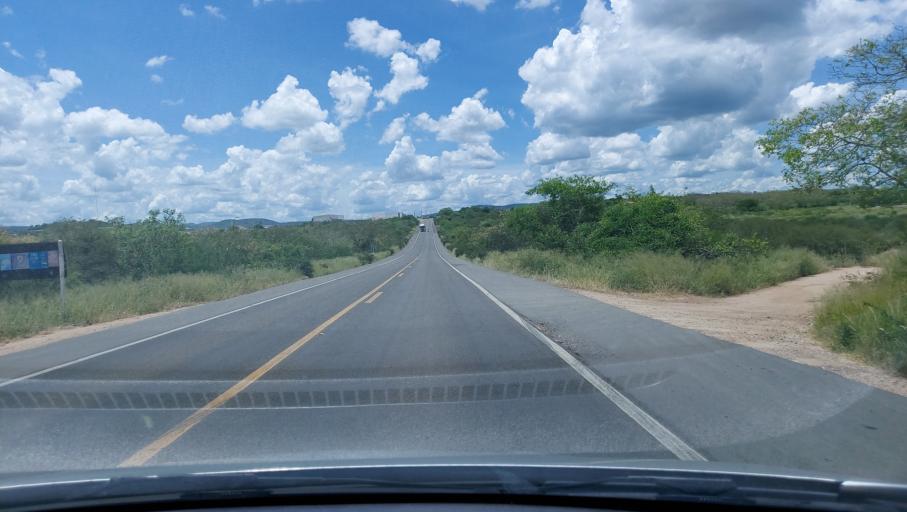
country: BR
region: Bahia
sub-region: Itaberaba
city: Itaberaba
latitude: -12.5207
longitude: -40.2699
